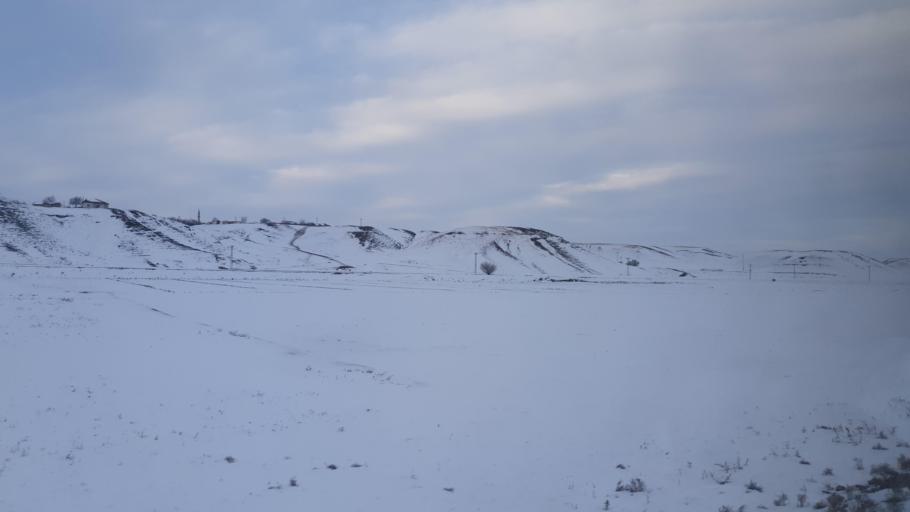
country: TR
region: Kirsehir
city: Mecidiye
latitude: 39.6866
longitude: 34.3933
